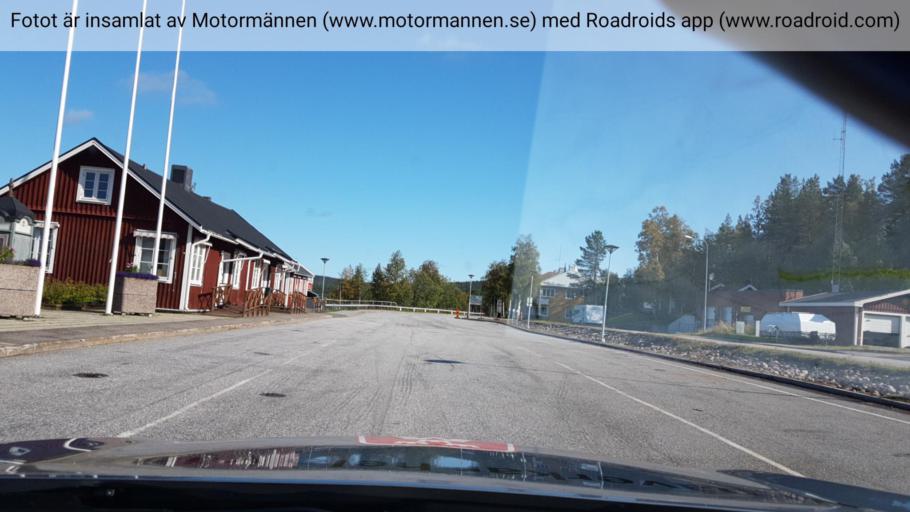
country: SE
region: Norrbotten
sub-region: Jokkmokks Kommun
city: Jokkmokk
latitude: 66.9568
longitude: 19.8060
